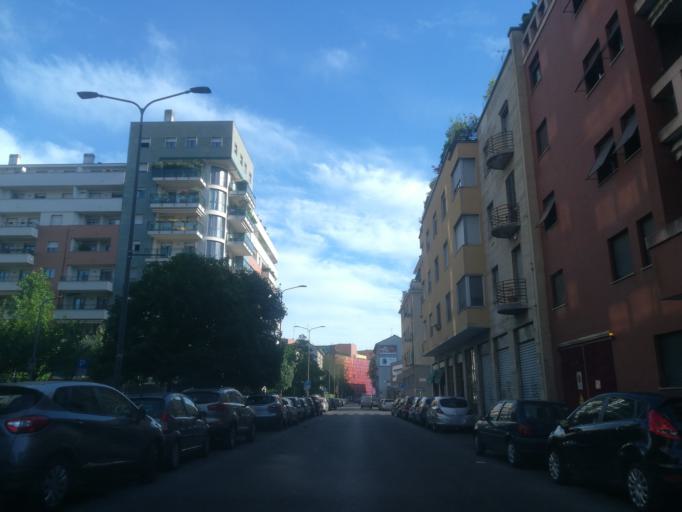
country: IT
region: Lombardy
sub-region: Citta metropolitana di Milano
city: Milano
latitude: 45.4994
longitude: 9.1815
